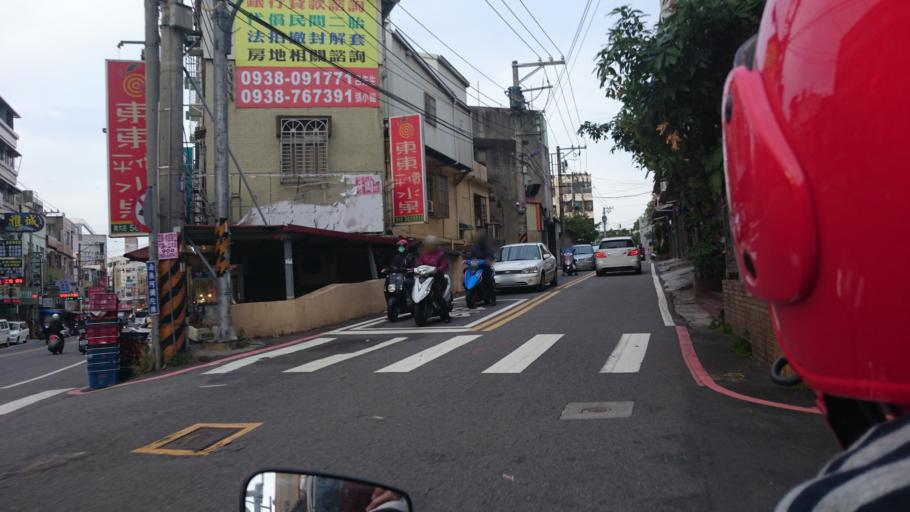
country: TW
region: Taiwan
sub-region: Hsinchu
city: Hsinchu
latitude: 24.7868
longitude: 120.9677
